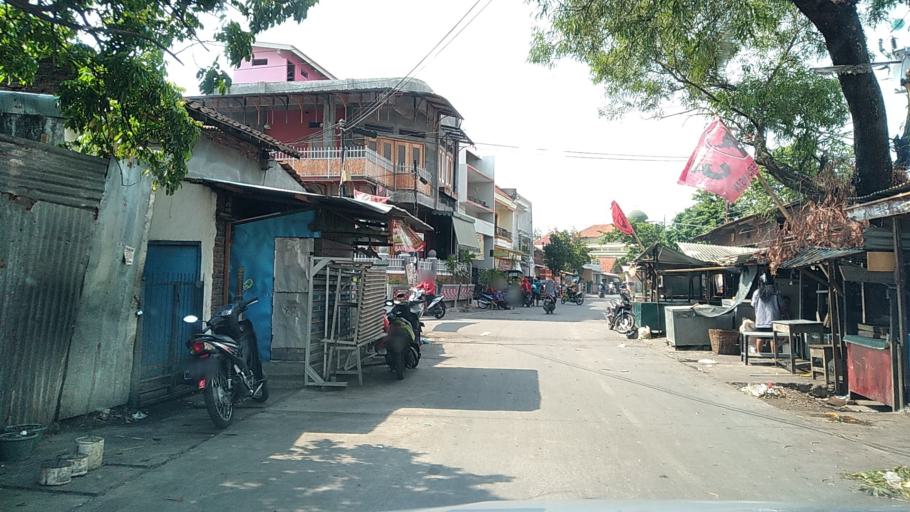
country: ID
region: Central Java
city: Semarang
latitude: -6.9745
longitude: 110.4401
